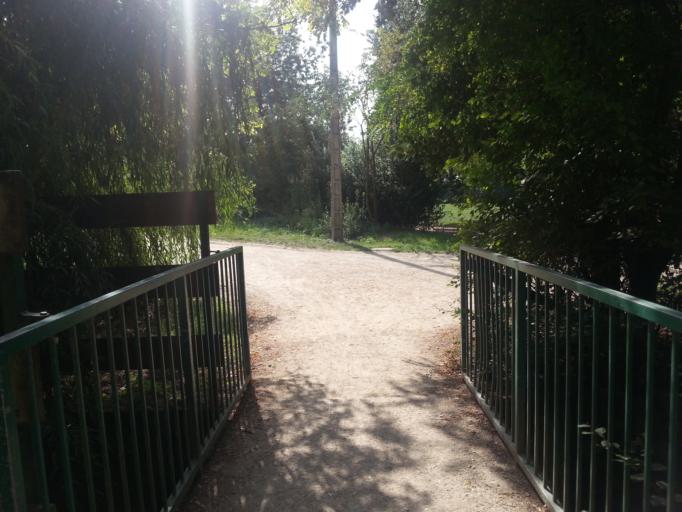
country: FR
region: Pays de la Loire
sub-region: Departement de la Sarthe
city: Le Mans
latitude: 47.9913
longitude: 0.1894
